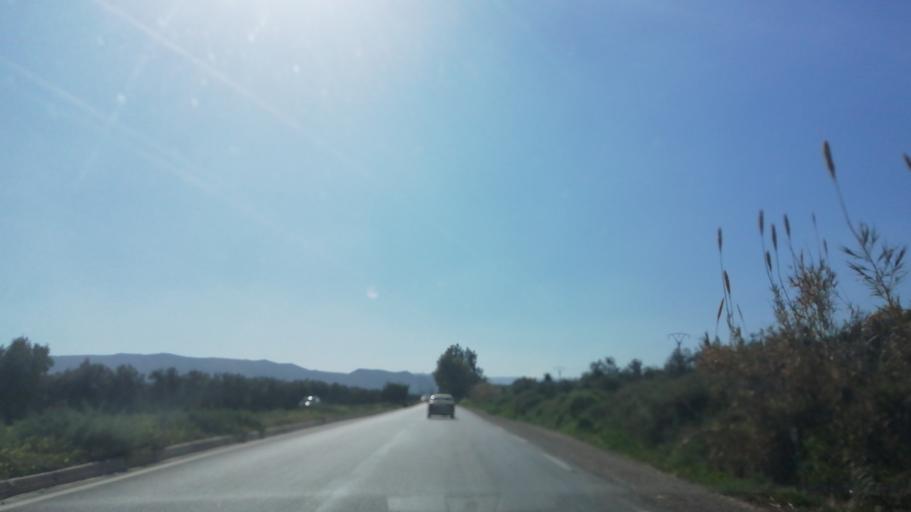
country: DZ
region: Mascara
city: Sig
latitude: 35.5498
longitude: -0.2061
